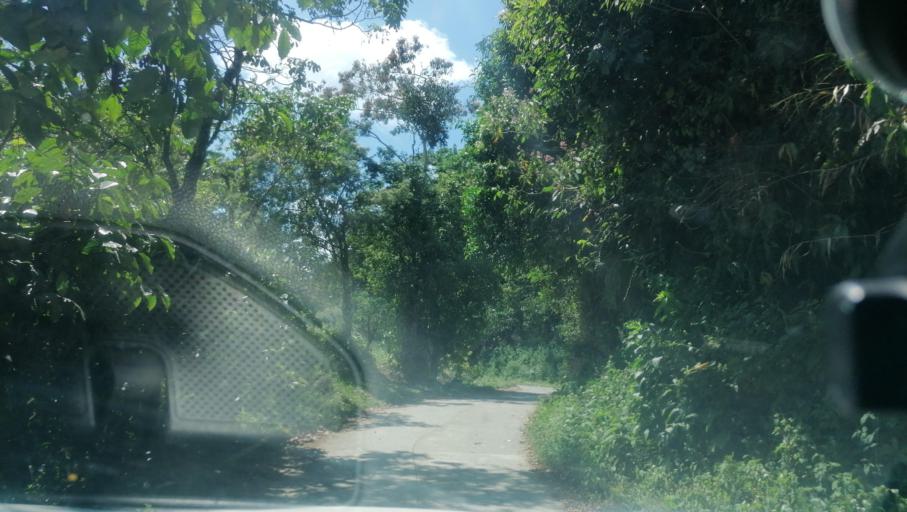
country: MX
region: Chiapas
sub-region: Union Juarez
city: Santo Domingo
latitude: 15.0655
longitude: -92.1405
